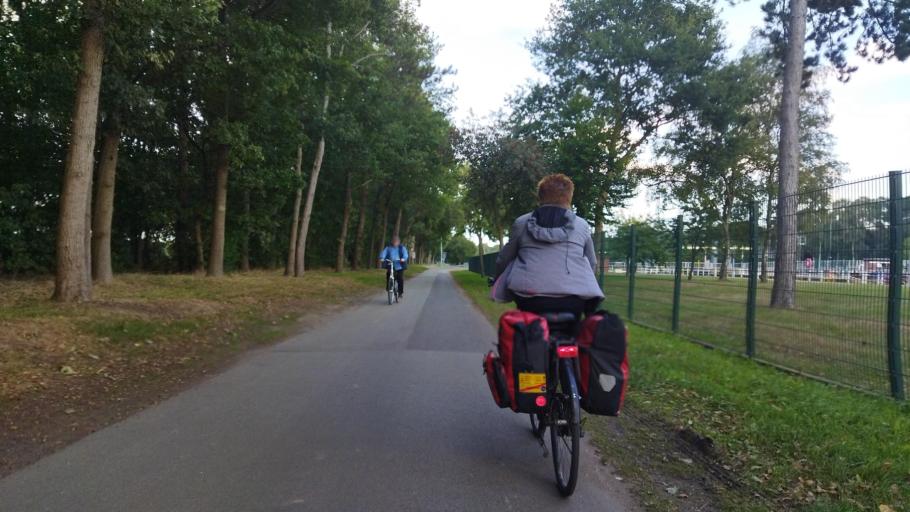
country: DE
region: Lower Saxony
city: Heede
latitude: 52.9848
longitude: 7.3127
